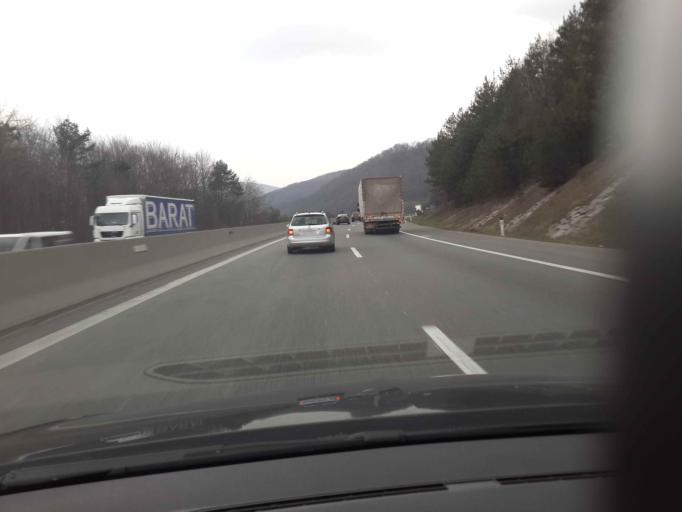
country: AT
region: Lower Austria
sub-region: Politischer Bezirk Baden
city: Alland
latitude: 48.0571
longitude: 16.1007
